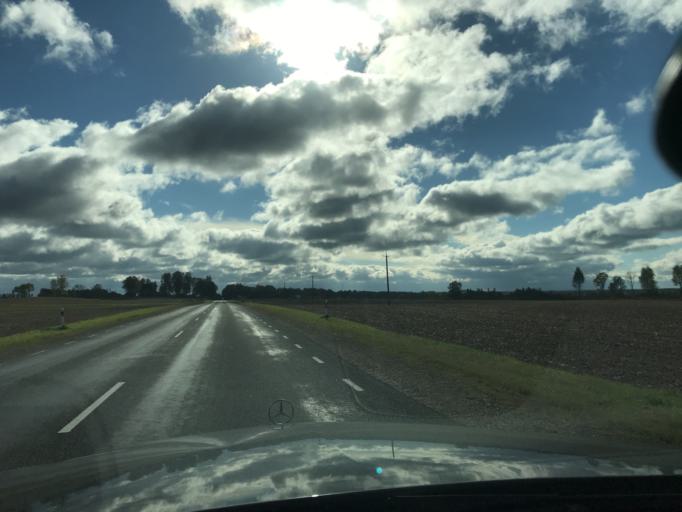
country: EE
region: Valgamaa
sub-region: Valga linn
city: Valga
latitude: 57.9698
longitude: 26.2624
